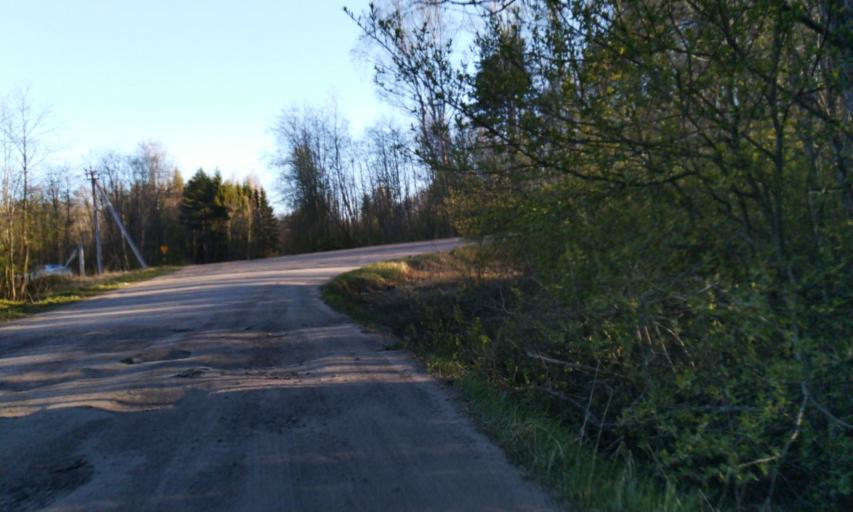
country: RU
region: Leningrad
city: Toksovo
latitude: 60.1388
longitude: 30.5704
